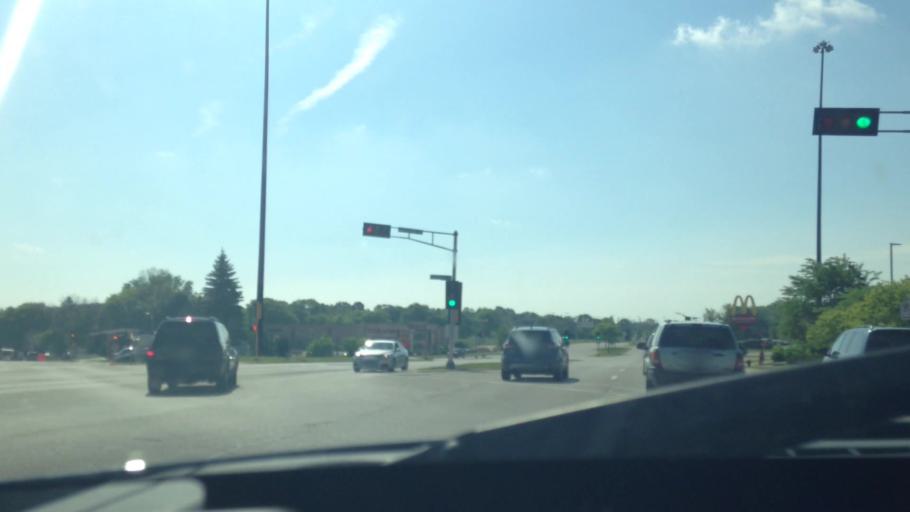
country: US
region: Wisconsin
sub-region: Waukesha County
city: Menomonee Falls
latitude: 43.1703
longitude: -88.1055
